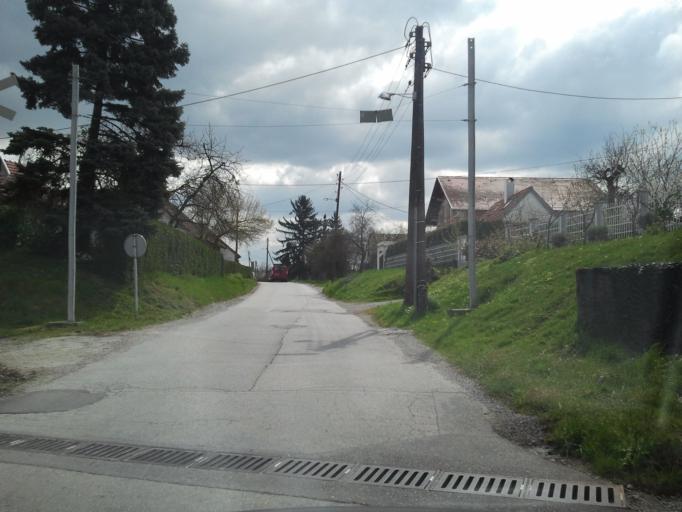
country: HR
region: Grad Zagreb
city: Brezovica
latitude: 45.7397
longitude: 15.8806
